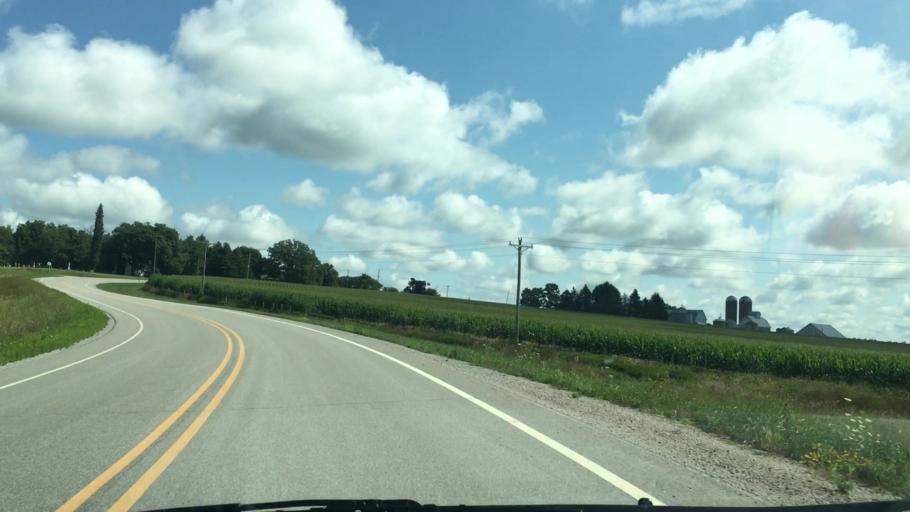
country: US
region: Iowa
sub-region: Johnson County
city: Solon
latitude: 41.8393
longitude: -91.4252
